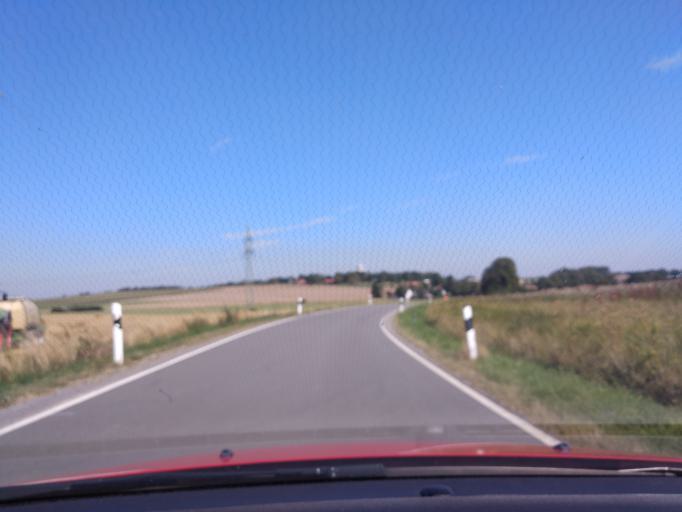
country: DE
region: North Rhine-Westphalia
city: Brakel
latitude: 51.6467
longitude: 9.2019
